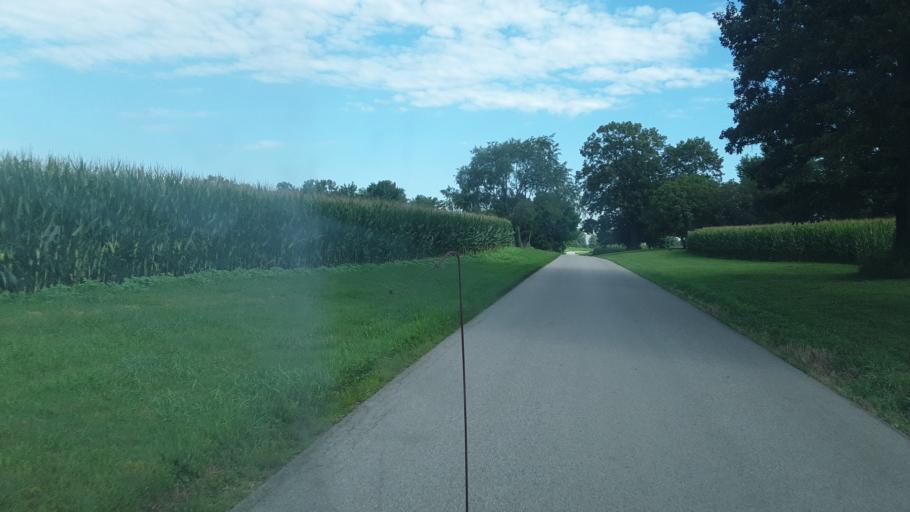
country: US
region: Kentucky
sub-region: Todd County
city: Guthrie
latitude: 36.6825
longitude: -87.1691
